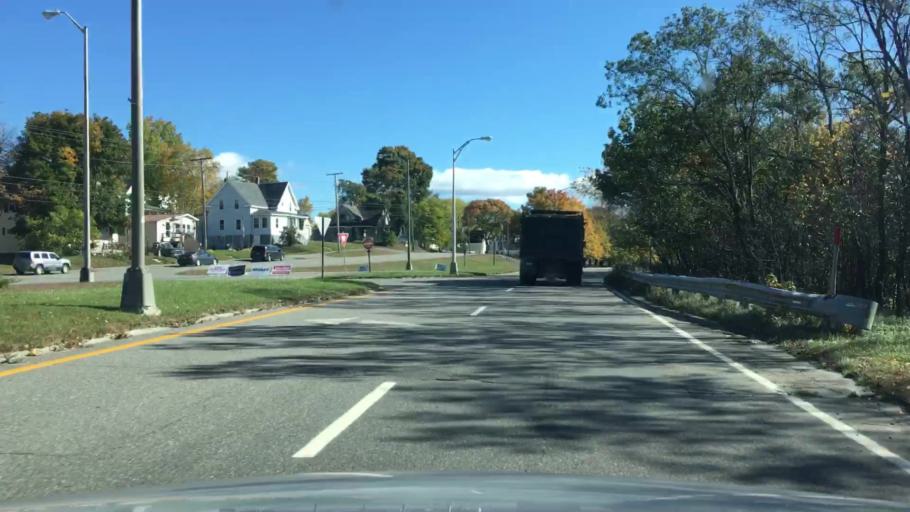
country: US
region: Maine
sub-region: Penobscot County
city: East Millinocket
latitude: 45.6250
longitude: -68.5727
